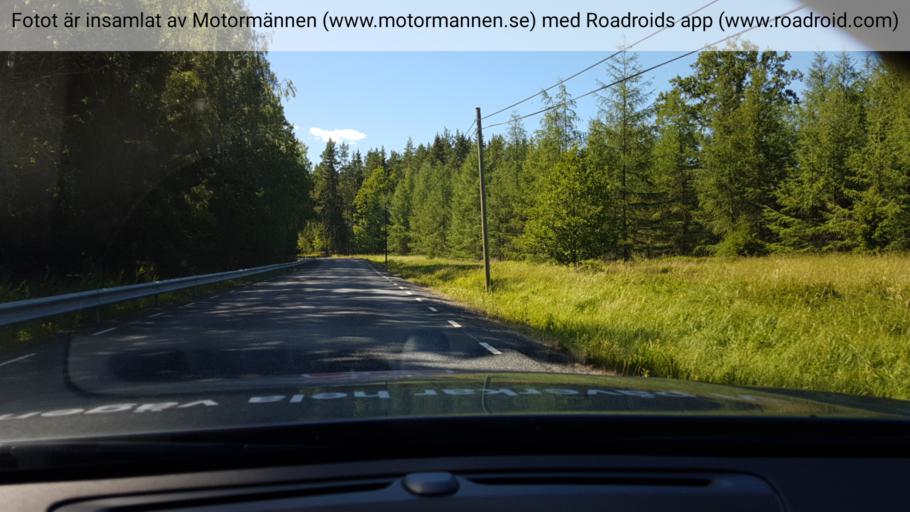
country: SE
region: Soedermanland
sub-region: Flens Kommun
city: Halleforsnas
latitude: 59.1709
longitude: 16.5503
